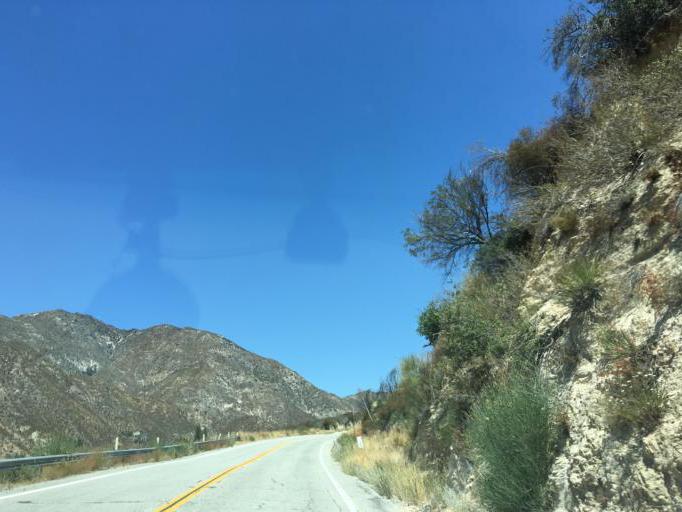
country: US
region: California
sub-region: Los Angeles County
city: La Crescenta-Montrose
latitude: 34.2870
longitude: -118.1913
